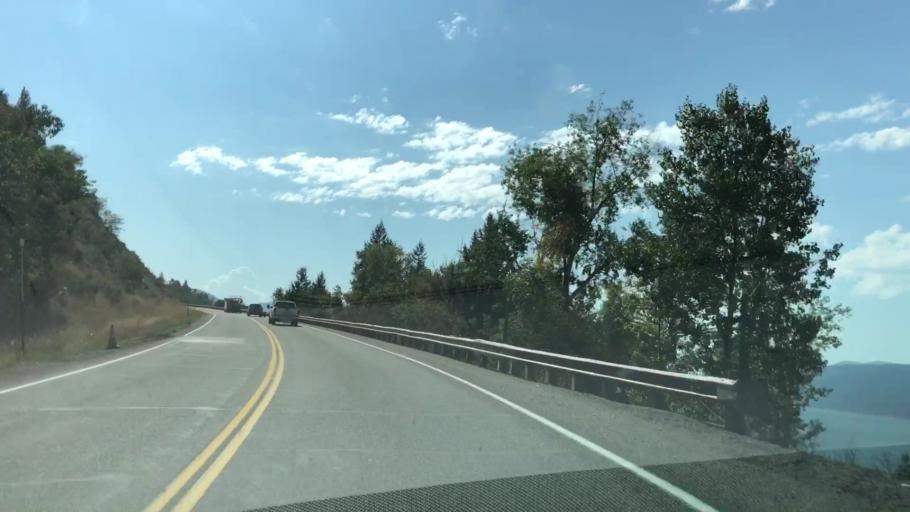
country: US
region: Idaho
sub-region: Teton County
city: Victor
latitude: 43.3134
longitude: -111.1462
